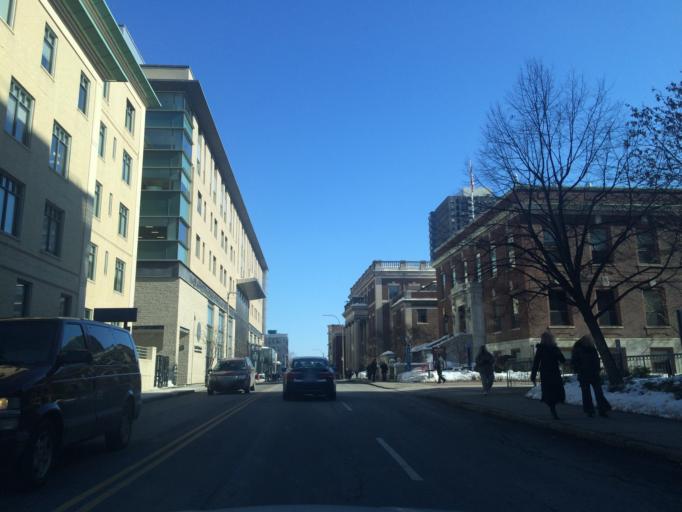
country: US
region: Massachusetts
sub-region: Norfolk County
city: Brookline
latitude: 42.3367
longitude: -71.1025
